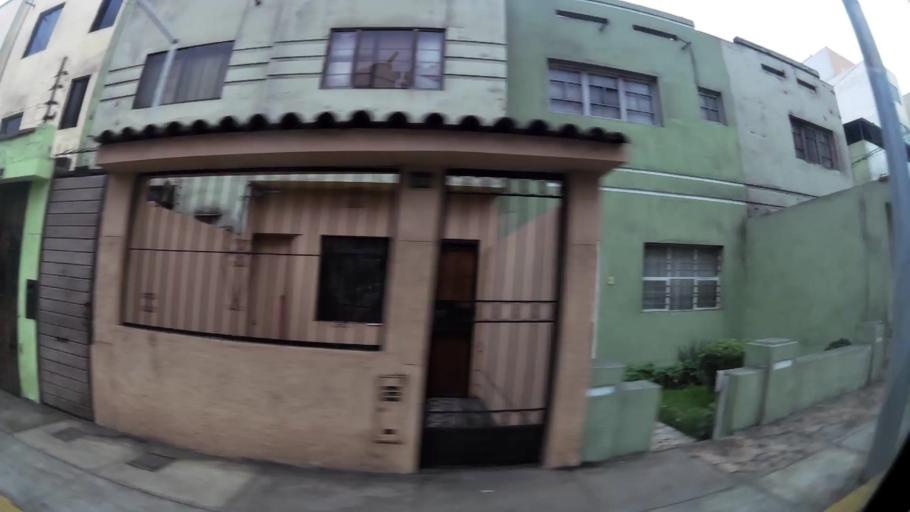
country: PE
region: Lima
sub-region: Lima
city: San Isidro
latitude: -12.0893
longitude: -77.0840
